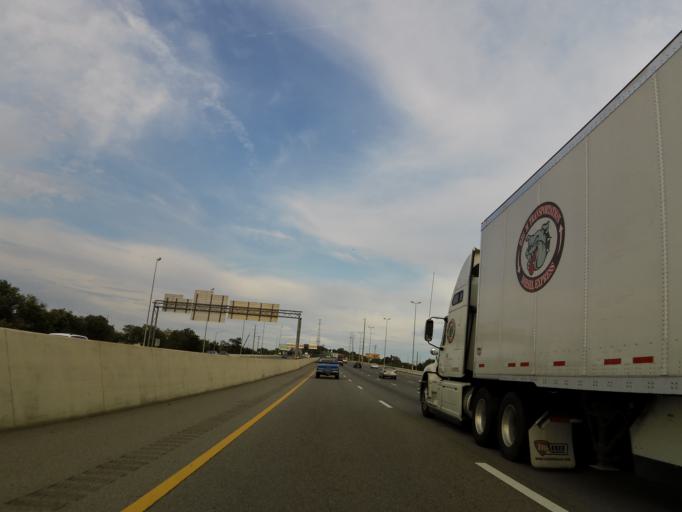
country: US
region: Tennessee
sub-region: Davidson County
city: Nashville
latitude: 36.1538
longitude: -86.8421
